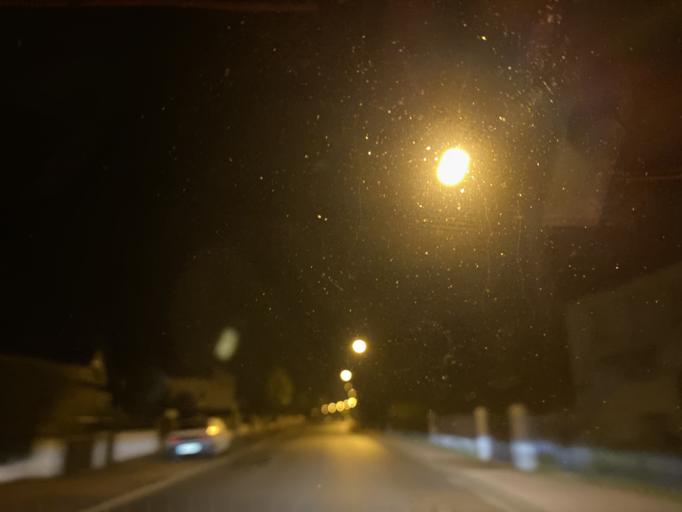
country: FR
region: Auvergne
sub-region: Departement de l'Allier
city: Abrest
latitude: 46.1053
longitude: 3.4400
